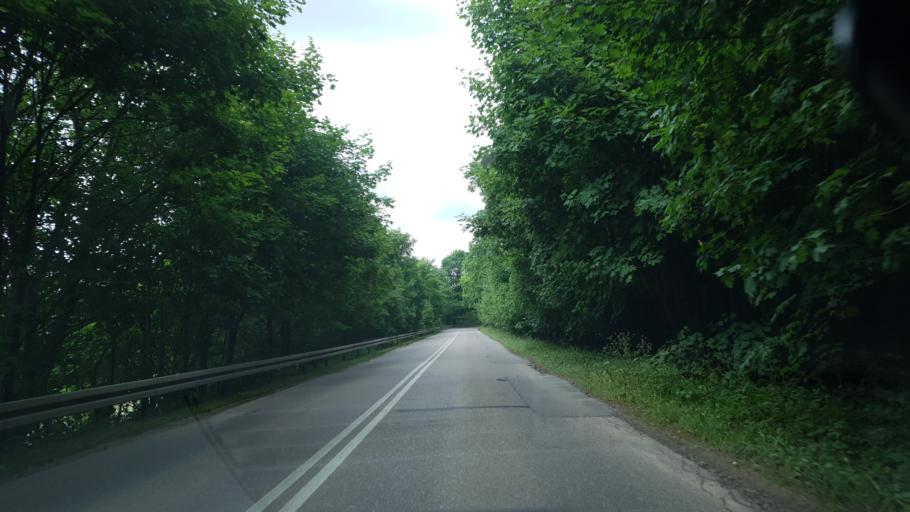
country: PL
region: Pomeranian Voivodeship
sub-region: Powiat kartuski
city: Przodkowo
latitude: 54.3681
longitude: 18.2719
